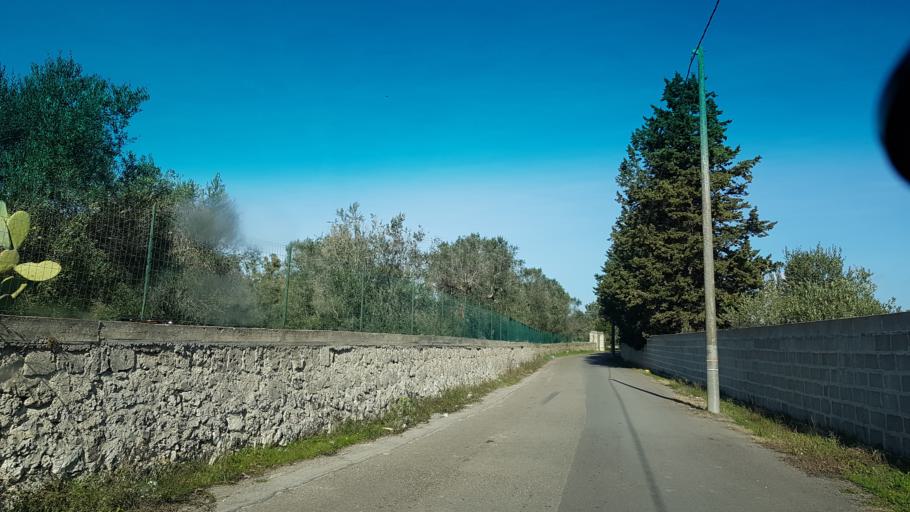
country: IT
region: Apulia
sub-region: Provincia di Lecce
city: Arnesano
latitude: 40.3566
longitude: 18.1052
